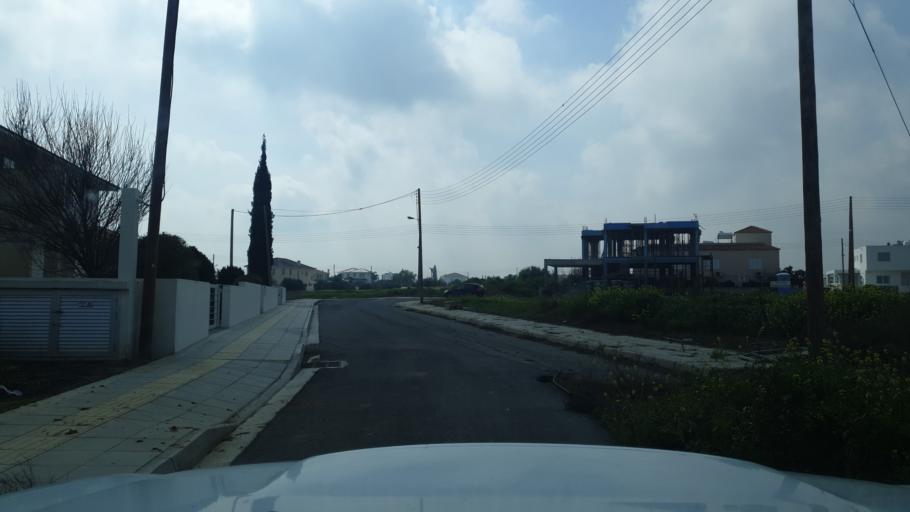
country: CY
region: Lefkosia
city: Kato Deftera
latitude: 35.0841
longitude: 33.2824
